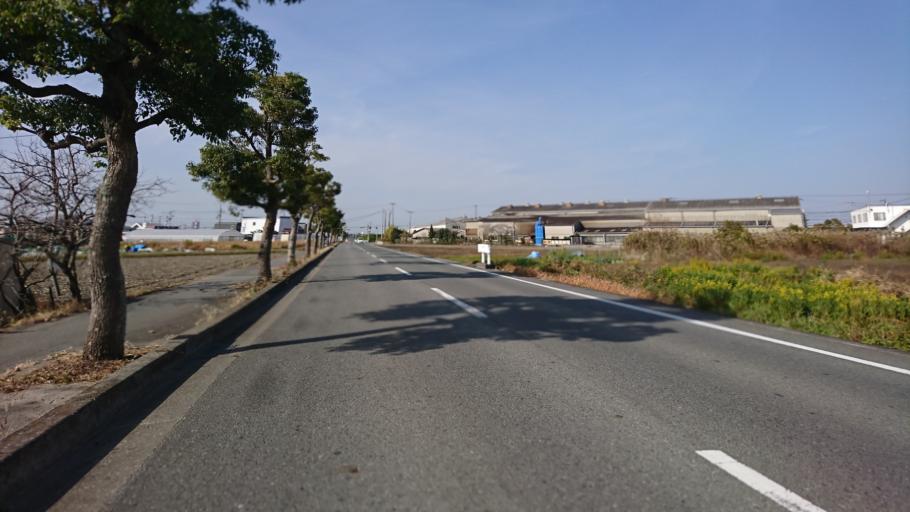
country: JP
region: Hyogo
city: Kakogawacho-honmachi
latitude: 34.7281
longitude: 134.8717
